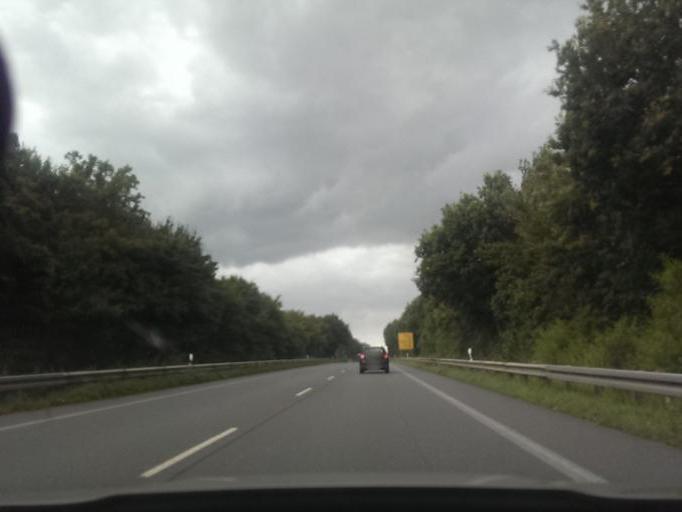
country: DE
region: North Rhine-Westphalia
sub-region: Regierungsbezirk Detmold
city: Steinheim
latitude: 51.8793
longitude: 9.0971
